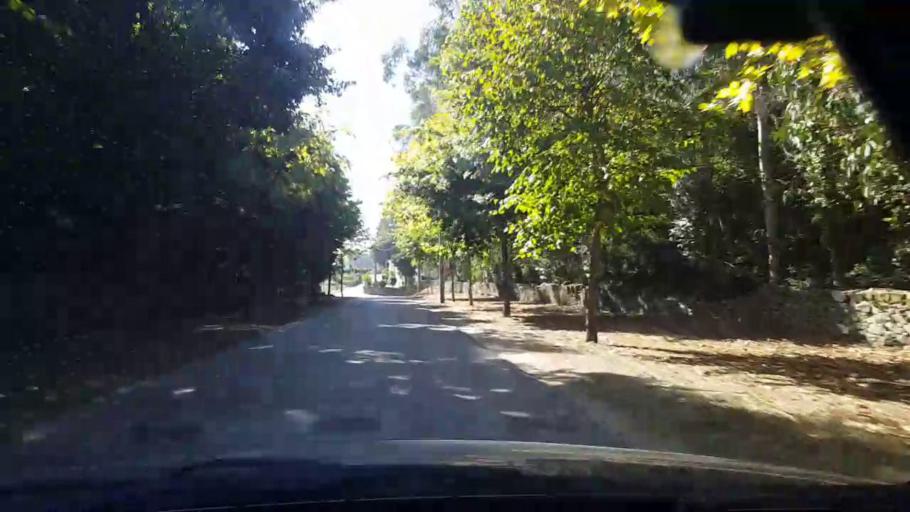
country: PT
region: Braga
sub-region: Vila Nova de Famalicao
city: Ribeirao
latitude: 41.3550
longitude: -8.6362
